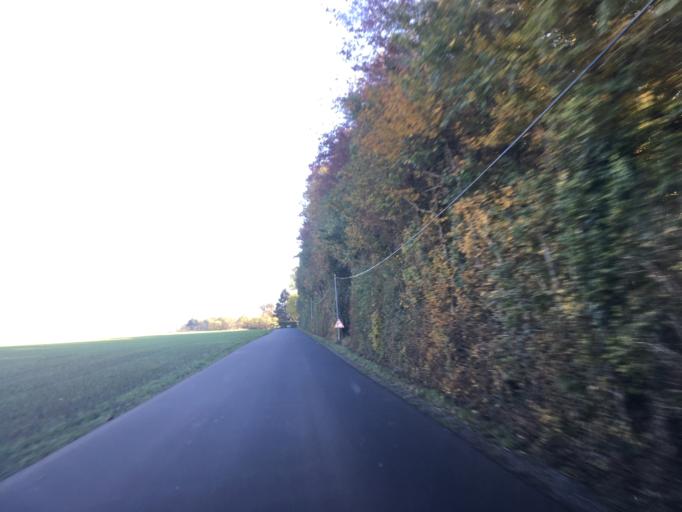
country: FR
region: Haute-Normandie
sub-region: Departement de l'Eure
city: Saint-Marcel
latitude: 49.0548
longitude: 1.4235
